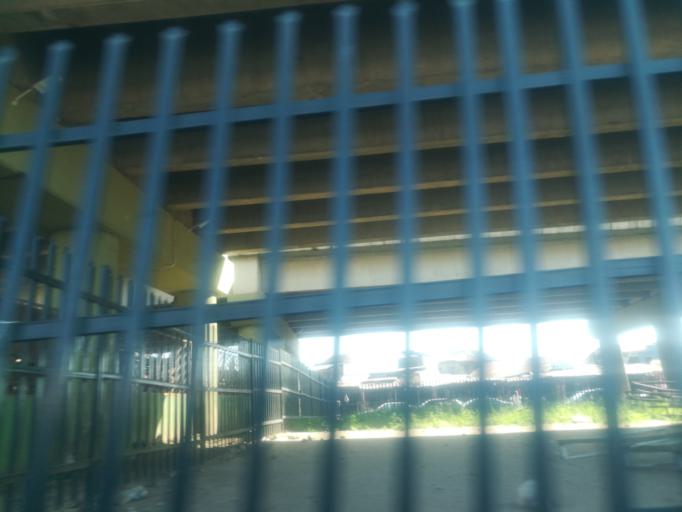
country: NG
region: Ogun
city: Abeokuta
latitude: 7.1571
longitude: 3.3423
